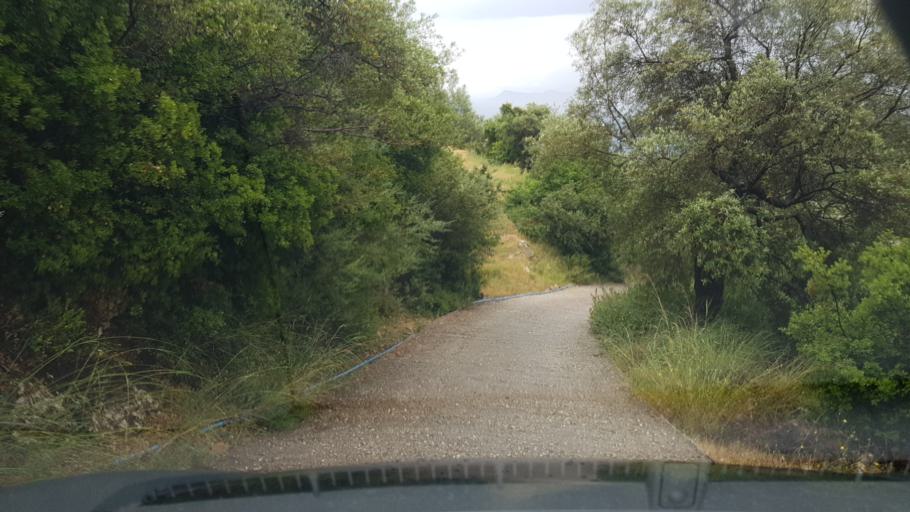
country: GR
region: Ionian Islands
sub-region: Lefkada
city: Nidri
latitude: 38.6514
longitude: 20.6839
